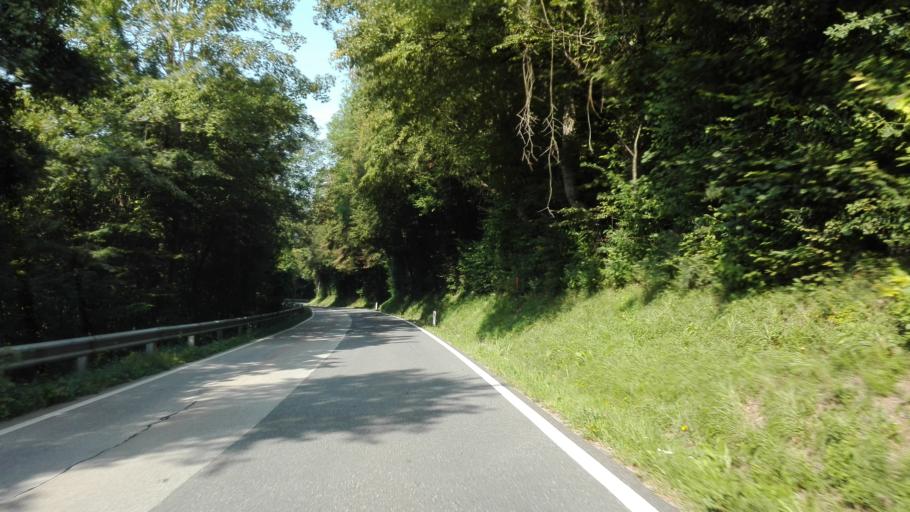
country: AT
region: Lower Austria
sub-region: Politischer Bezirk Sankt Polten
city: Rabenstein an der Pielach
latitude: 48.0346
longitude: 15.4902
